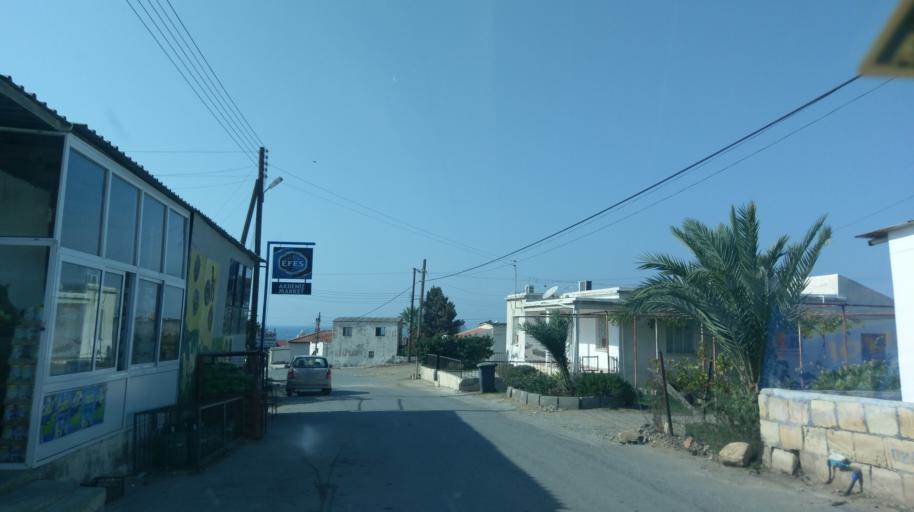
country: CY
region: Lefkosia
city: Morfou
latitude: 35.2990
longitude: 32.9645
